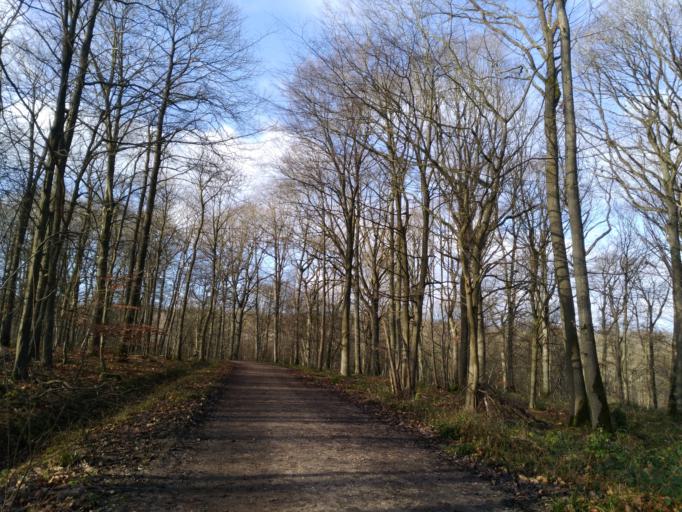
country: FR
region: Ile-de-France
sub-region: Departement des Yvelines
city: Elancourt
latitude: 48.8026
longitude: 1.9361
